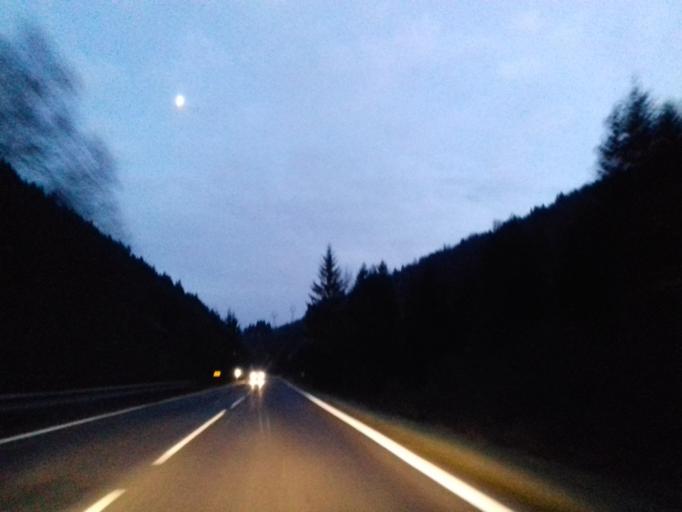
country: SK
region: Zilinsky
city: Ruzomberok
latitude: 48.9222
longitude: 19.2602
